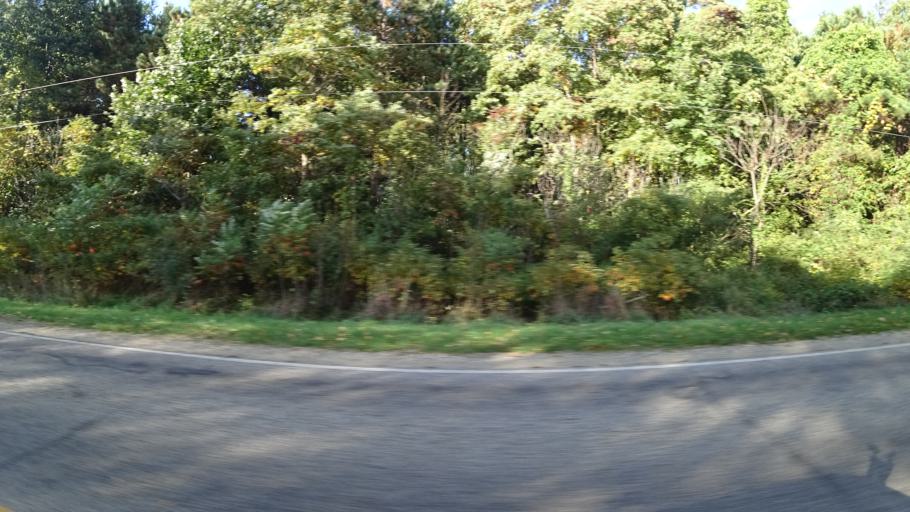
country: US
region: Michigan
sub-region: Saint Joseph County
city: Centreville
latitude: 41.8535
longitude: -85.5028
